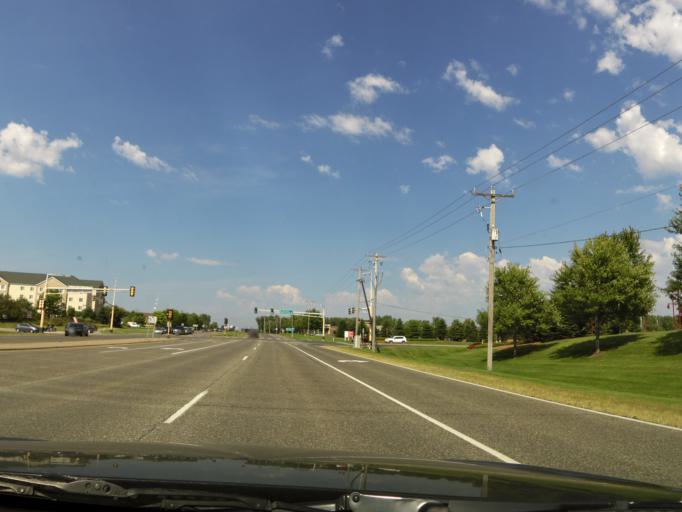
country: US
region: Minnesota
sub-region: Washington County
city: Oakdale
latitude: 44.9515
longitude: -92.9341
